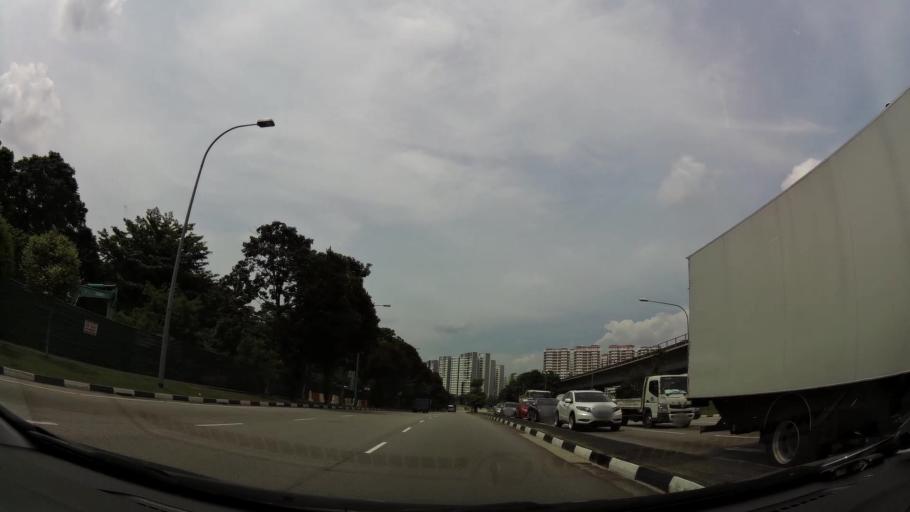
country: MY
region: Johor
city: Johor Bahru
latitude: 1.3693
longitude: 103.7481
